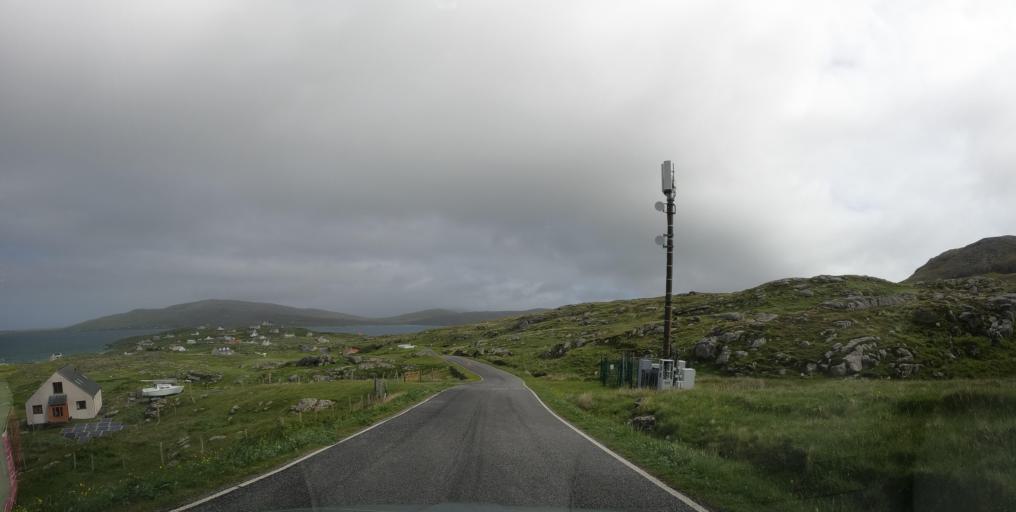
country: GB
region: Scotland
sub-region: Eilean Siar
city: Isle of South Uist
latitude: 57.0788
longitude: -7.3025
